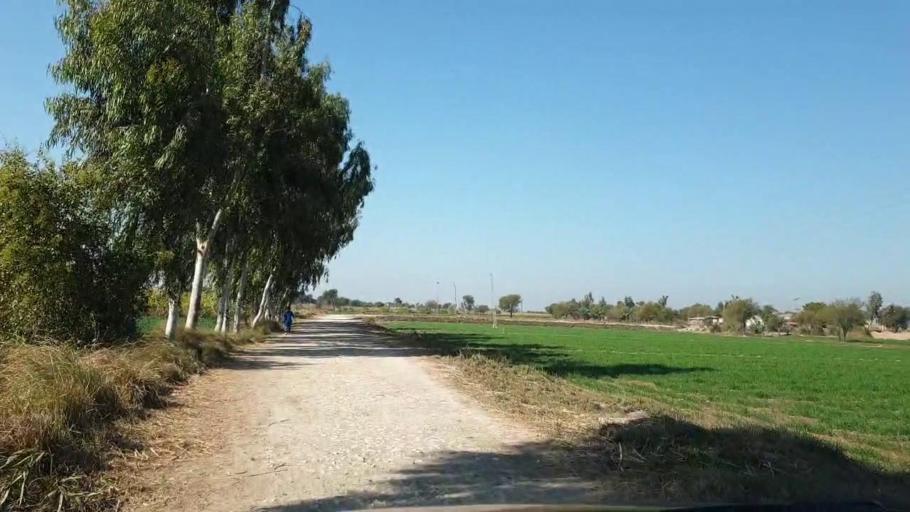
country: PK
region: Sindh
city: Sinjhoro
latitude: 26.1099
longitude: 68.8413
